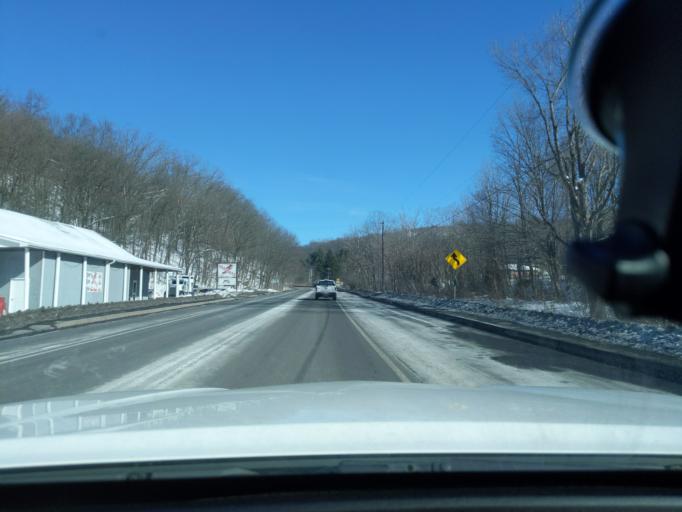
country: US
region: Maryland
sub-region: Allegany County
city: Lonaconing
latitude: 39.5906
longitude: -78.9454
